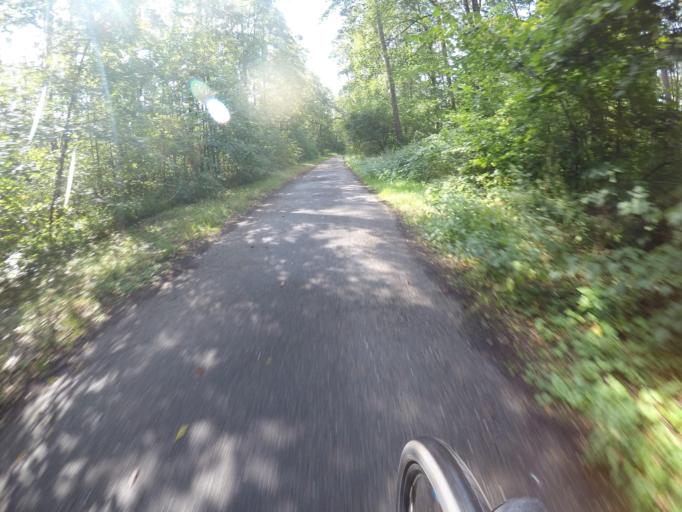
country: DE
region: Baden-Wuerttemberg
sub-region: Karlsruhe Region
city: Hockenheim
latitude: 49.3517
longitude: 8.5565
